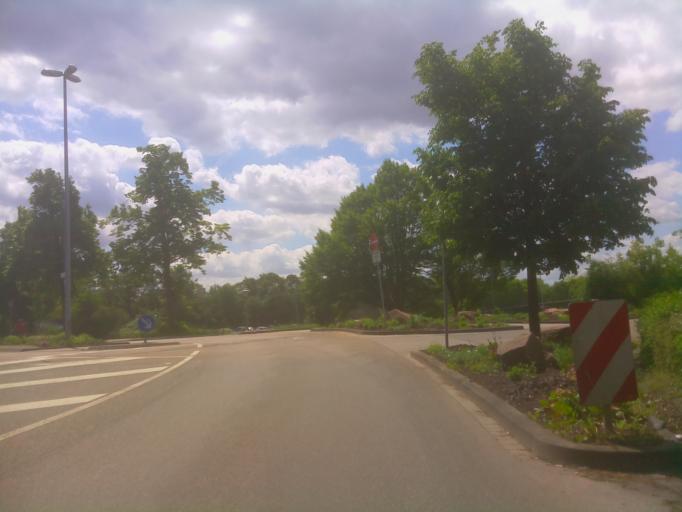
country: DE
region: Rheinland-Pfalz
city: Speyer
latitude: 49.3156
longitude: 8.4460
